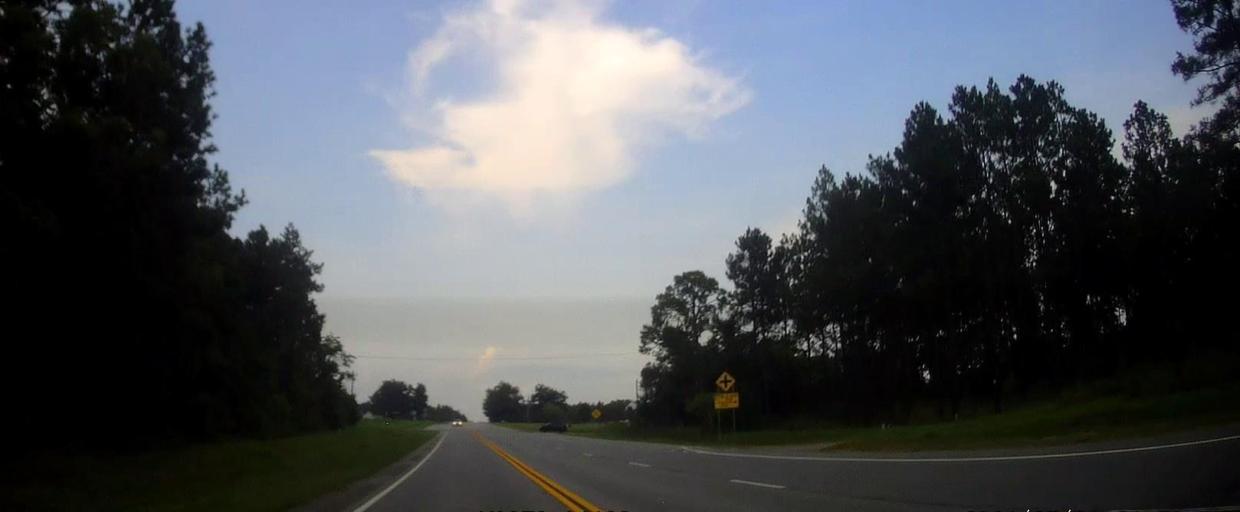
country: US
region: Georgia
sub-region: Laurens County
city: East Dublin
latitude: 32.6162
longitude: -82.8150
